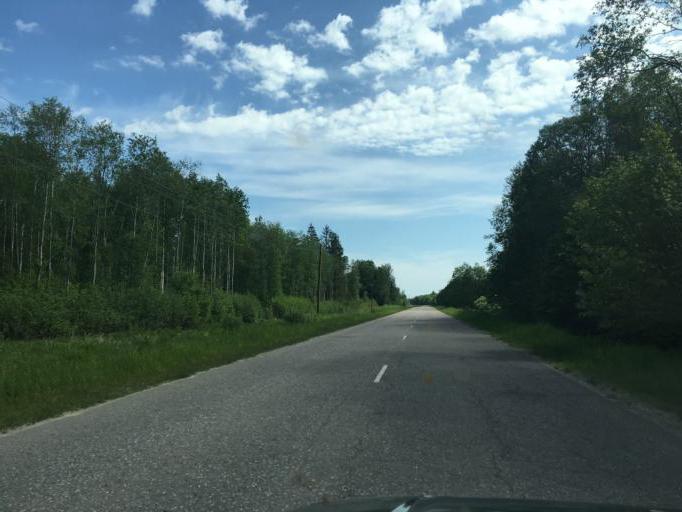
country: LV
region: Talsu Rajons
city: Valdemarpils
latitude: 57.3734
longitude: 22.4896
